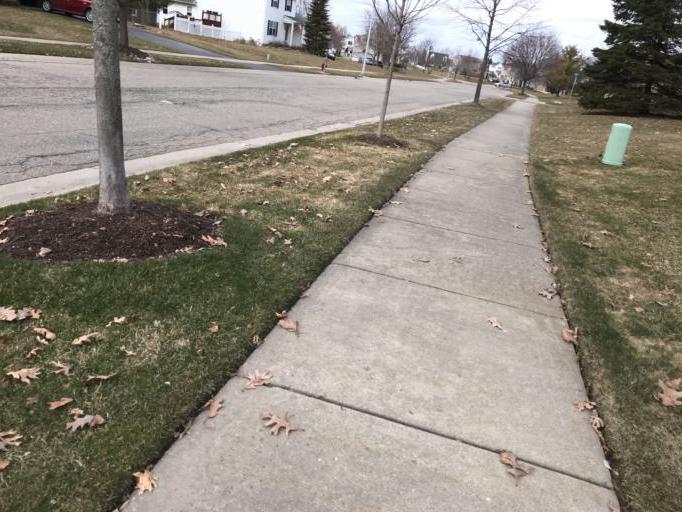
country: US
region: Michigan
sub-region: Oakland County
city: South Lyon
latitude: 42.4699
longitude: -83.6409
